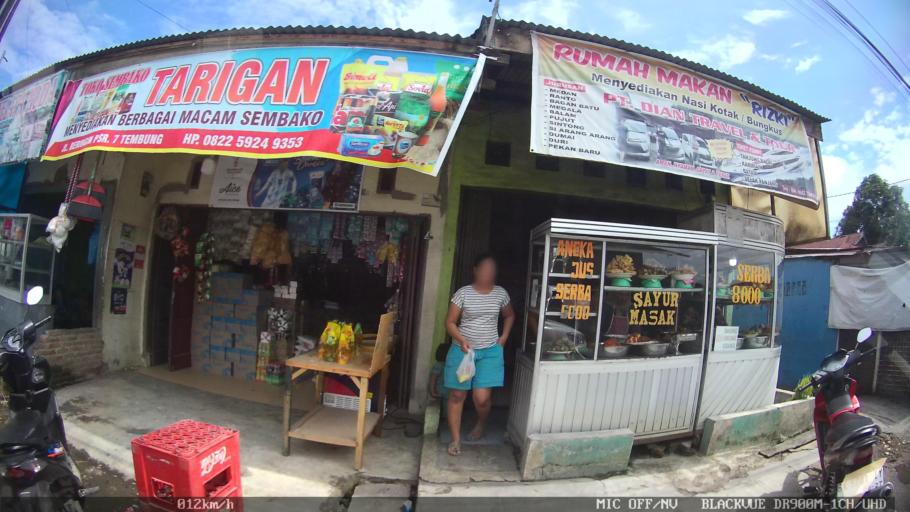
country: ID
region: North Sumatra
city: Medan
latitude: 3.5911
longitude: 98.7465
